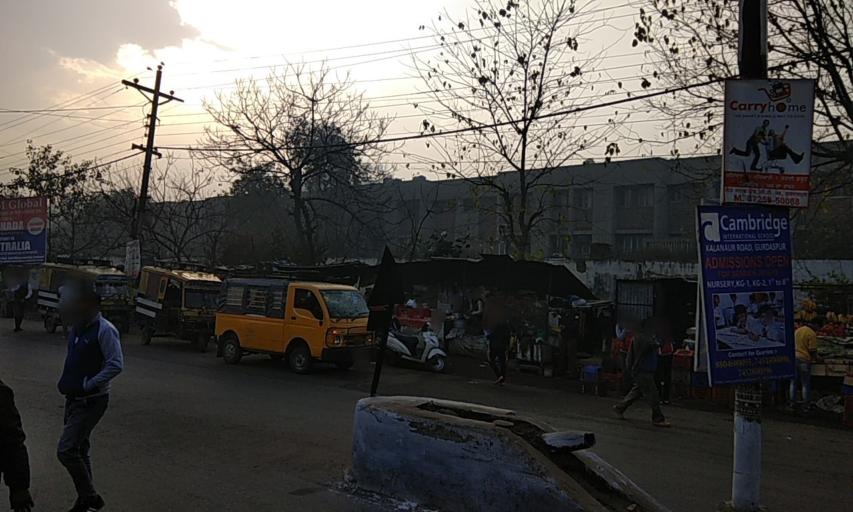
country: IN
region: Punjab
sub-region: Gurdaspur
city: Gurdaspur
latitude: 32.0414
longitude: 75.4067
